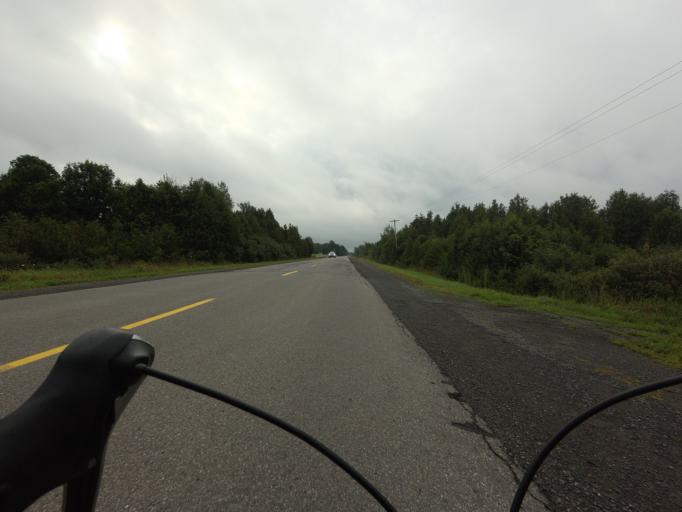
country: CA
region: Ontario
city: Bells Corners
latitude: 45.1558
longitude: -75.7892
